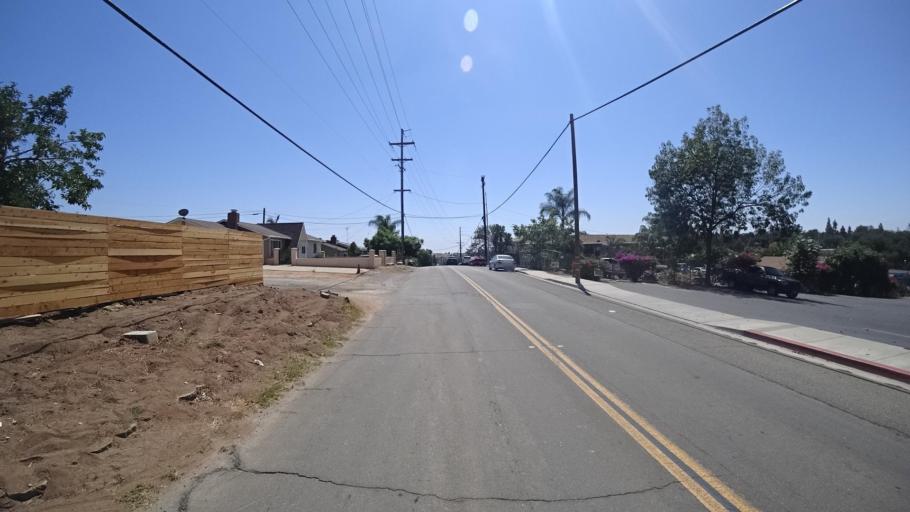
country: US
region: California
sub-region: San Diego County
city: Fallbrook
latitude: 33.3709
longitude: -117.2493
